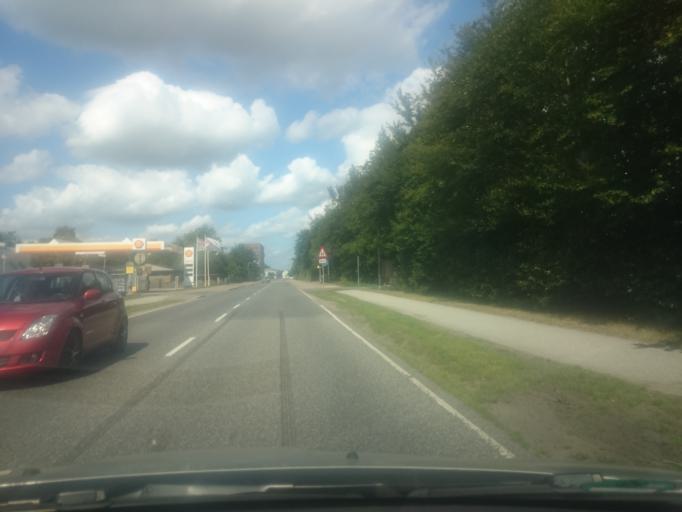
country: DK
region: South Denmark
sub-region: Billund Kommune
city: Billund
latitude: 55.7275
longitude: 9.1217
